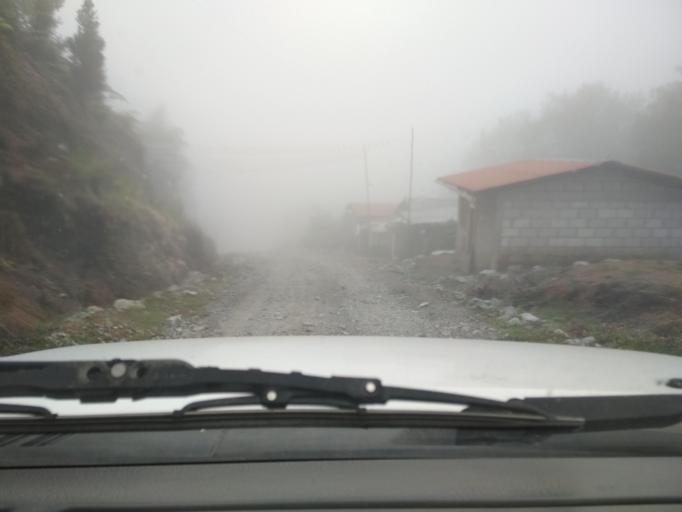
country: MX
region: Veracruz
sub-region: La Perla
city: Barrio de San Miguel
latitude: 18.9457
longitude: -97.1212
